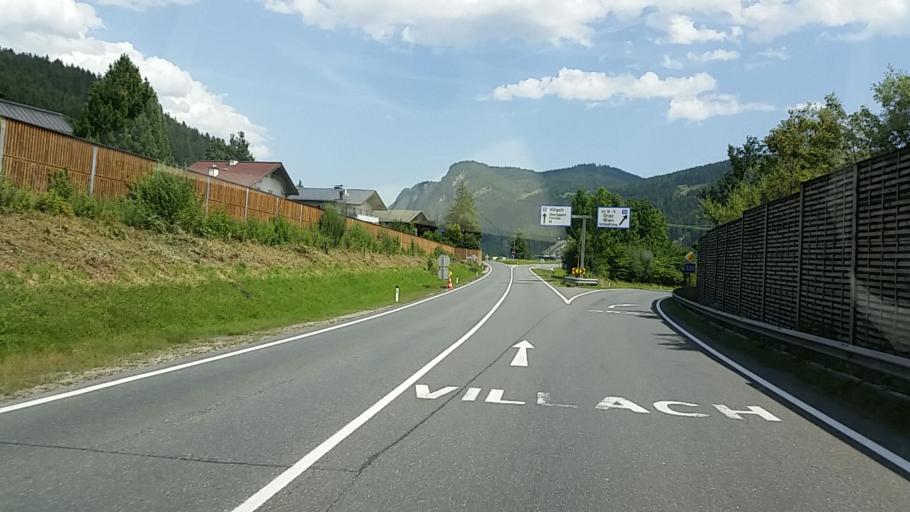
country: AT
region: Salzburg
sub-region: Politischer Bezirk Sankt Johann im Pongau
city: Radstadt
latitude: 47.3858
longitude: 13.4691
